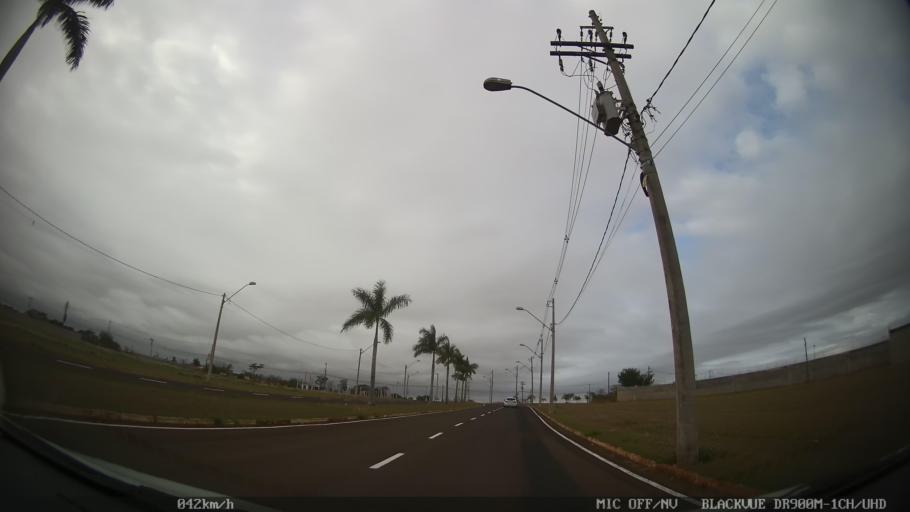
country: BR
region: Sao Paulo
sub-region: Sao Jose Do Rio Preto
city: Sao Jose do Rio Preto
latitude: -20.8254
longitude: -49.4173
